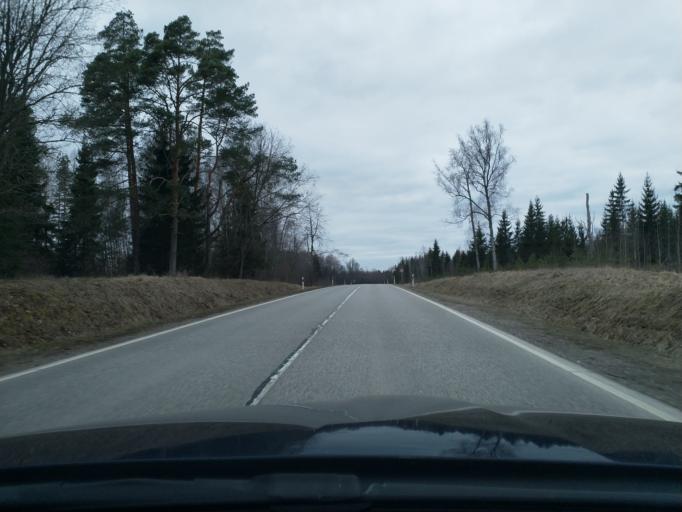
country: LV
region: Kuldigas Rajons
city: Kuldiga
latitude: 56.9574
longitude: 22.1153
